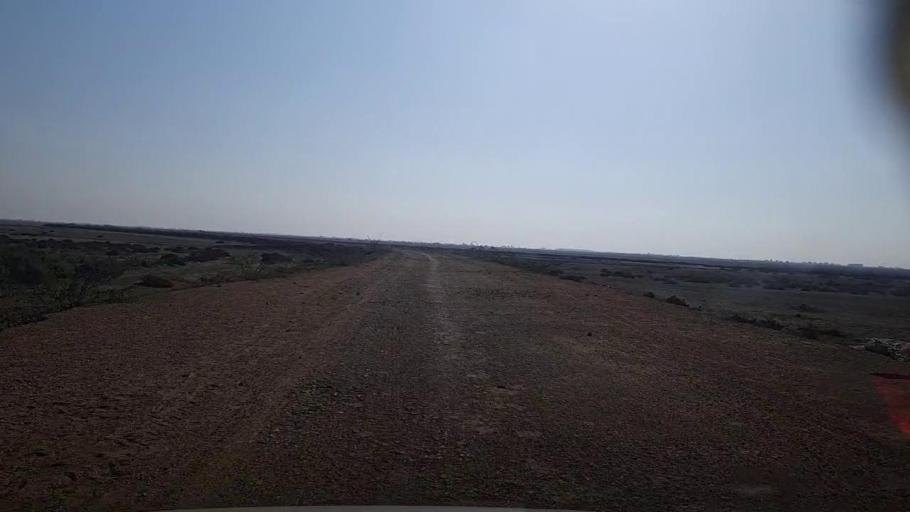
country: PK
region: Sindh
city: Mirpur Sakro
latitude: 24.5175
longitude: 67.4933
